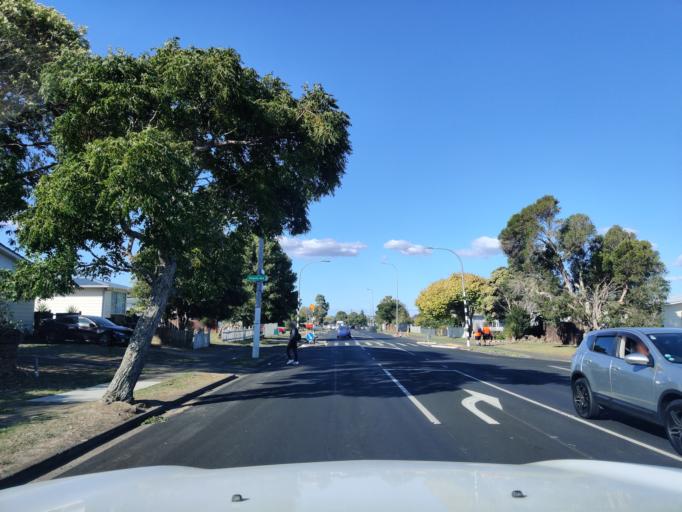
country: NZ
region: Auckland
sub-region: Auckland
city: Takanini
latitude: -37.0381
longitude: 174.8877
